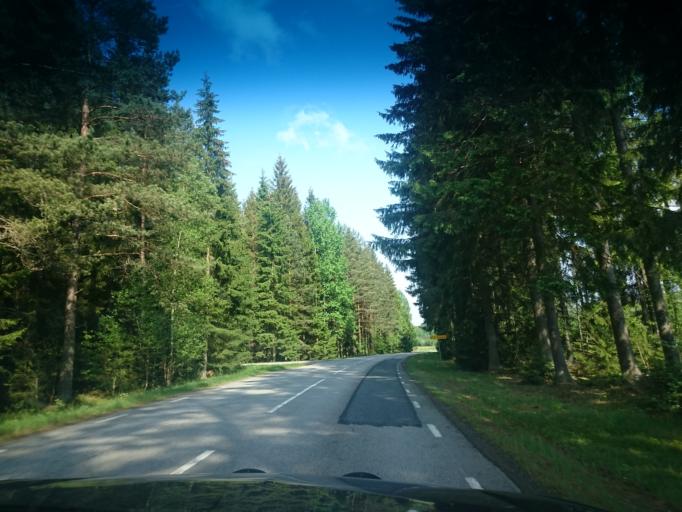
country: SE
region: Joenkoeping
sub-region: Vetlanda Kommun
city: Vetlanda
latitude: 57.3814
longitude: 15.0122
